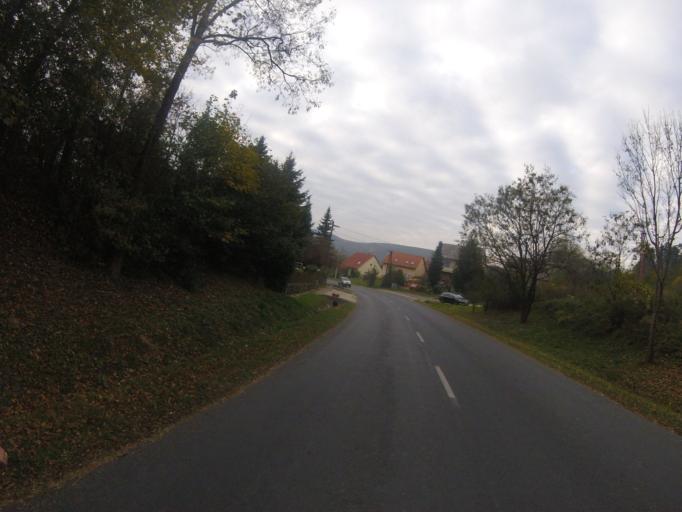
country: HU
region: Veszprem
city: Herend
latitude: 47.2566
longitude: 17.7328
